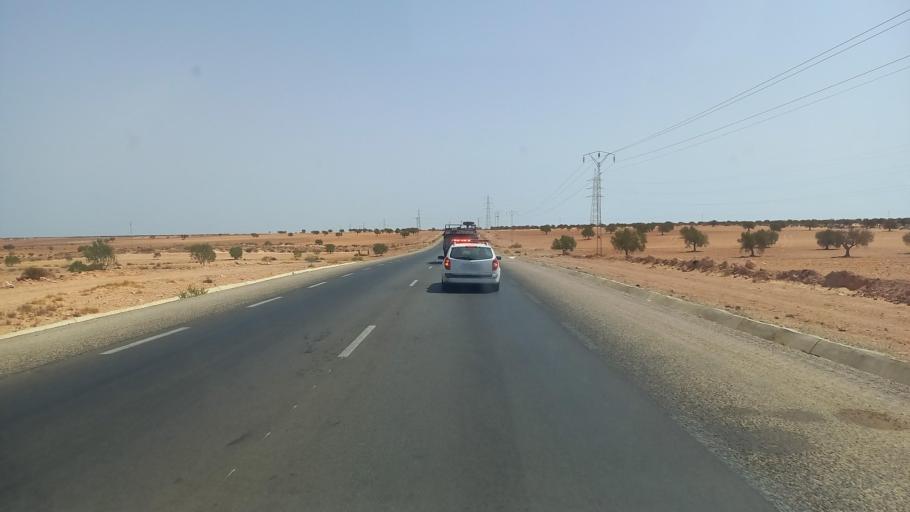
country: TN
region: Madanin
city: Zarzis
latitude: 33.4034
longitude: 10.8496
